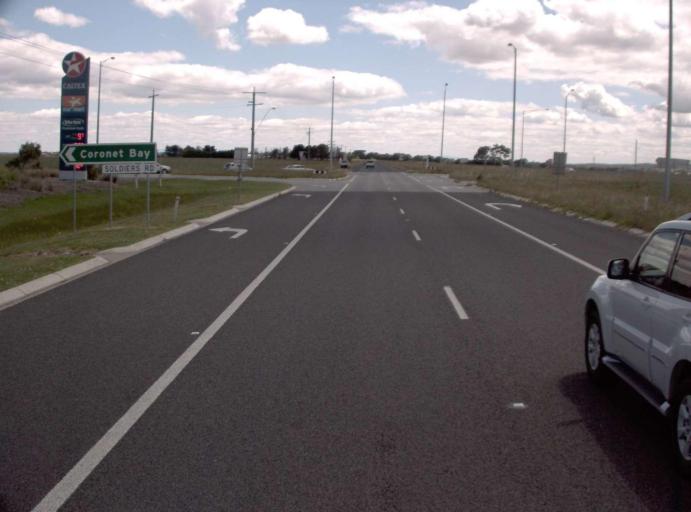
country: AU
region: Victoria
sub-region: Bass Coast
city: North Wonthaggi
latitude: -38.4731
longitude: 145.4743
